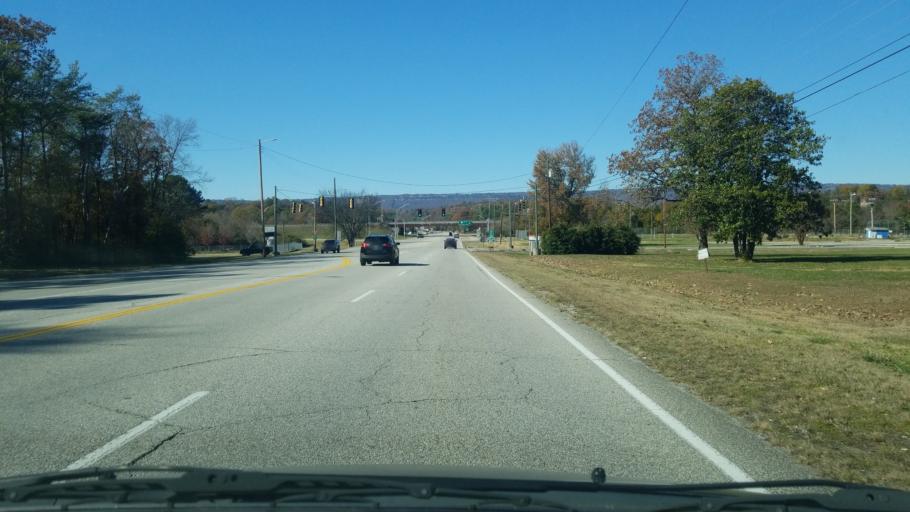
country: US
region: Tennessee
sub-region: Hamilton County
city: East Chattanooga
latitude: 35.1106
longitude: -85.2474
